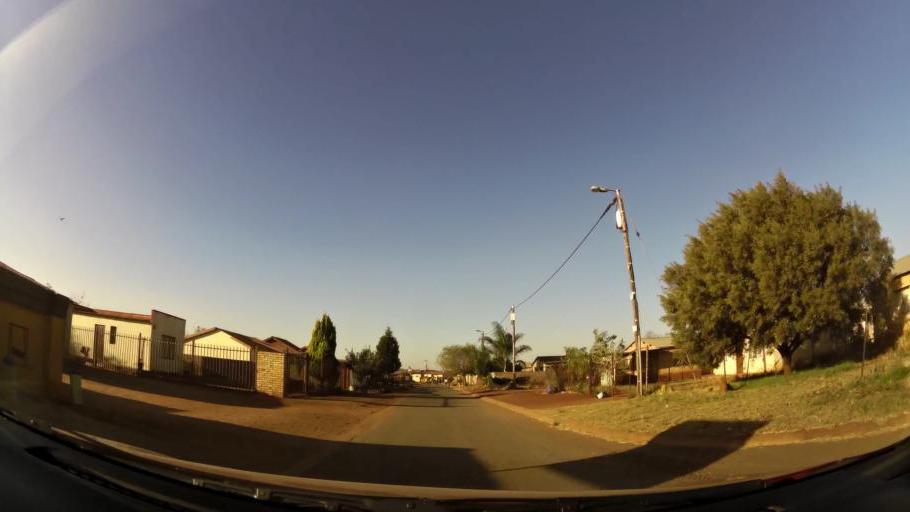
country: ZA
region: Gauteng
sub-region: City of Tshwane Metropolitan Municipality
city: Mabopane
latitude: -25.5948
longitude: 28.1059
